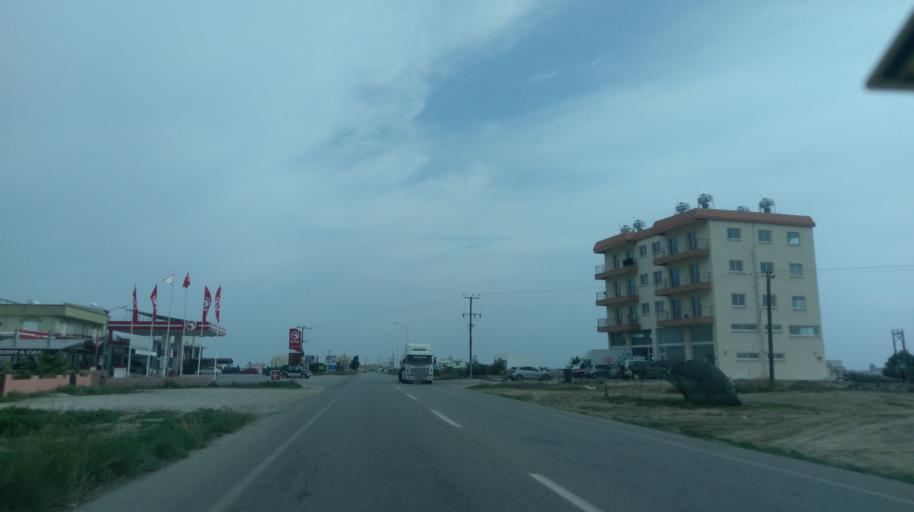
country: CY
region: Ammochostos
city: Trikomo
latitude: 35.2788
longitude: 33.8902
